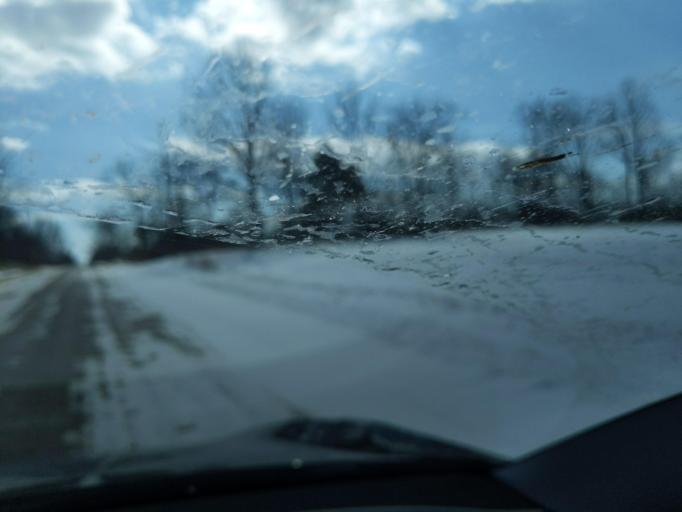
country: US
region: Michigan
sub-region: Livingston County
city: Fowlerville
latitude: 42.6180
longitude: -84.0910
